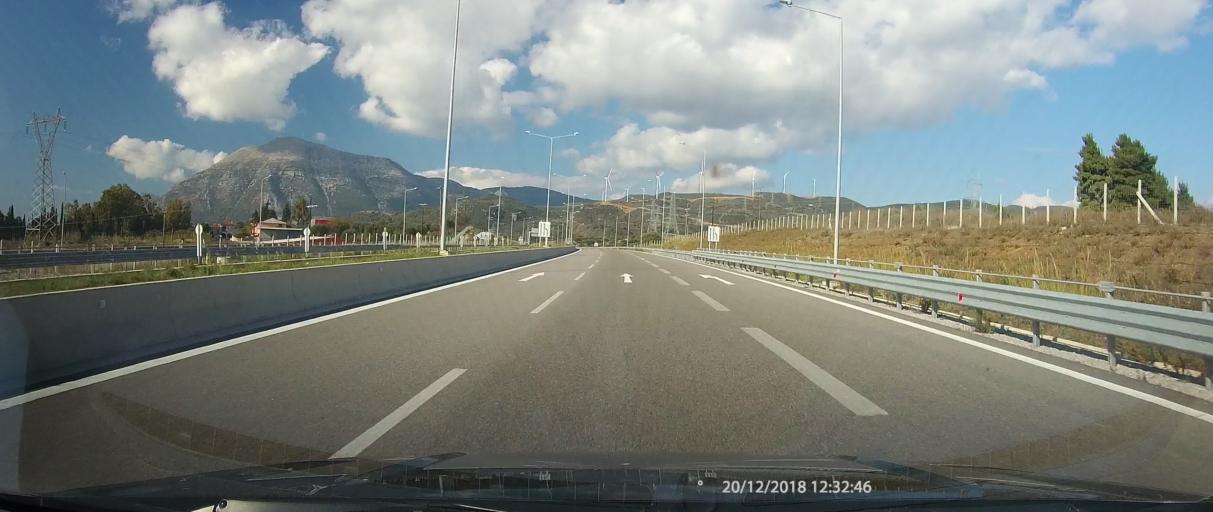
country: GR
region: West Greece
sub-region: Nomos Aitolias kai Akarnanias
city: Antirrio
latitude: 38.3432
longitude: 21.7587
